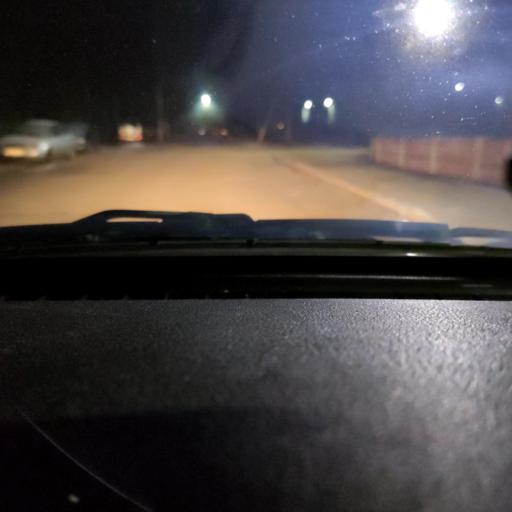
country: RU
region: Voronezj
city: Novaya Usman'
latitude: 51.6524
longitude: 39.3354
